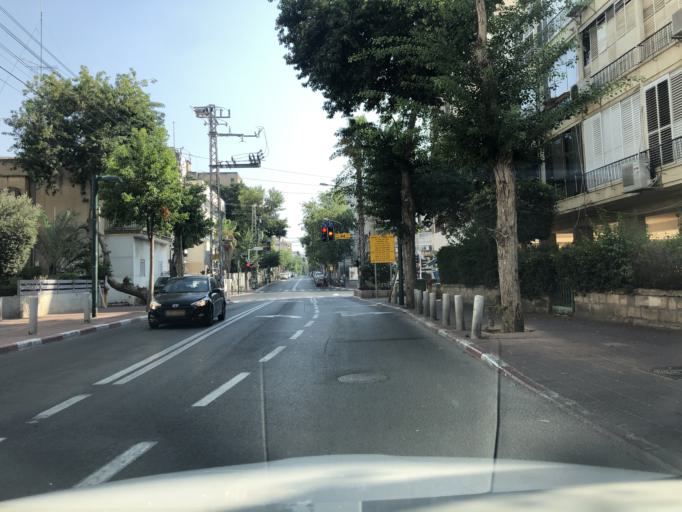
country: IL
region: Tel Aviv
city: Ramat Gan
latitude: 32.0846
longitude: 34.8195
